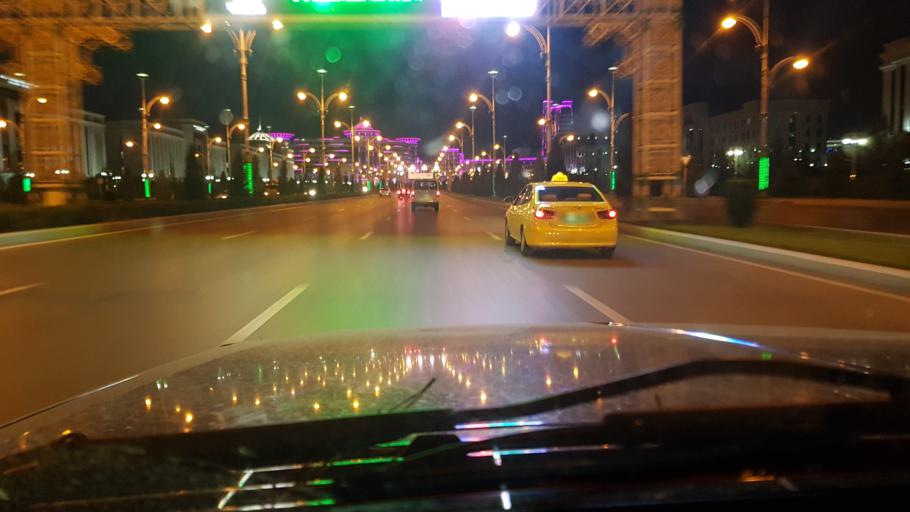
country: TM
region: Ahal
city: Ashgabat
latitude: 37.8981
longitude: 58.3633
